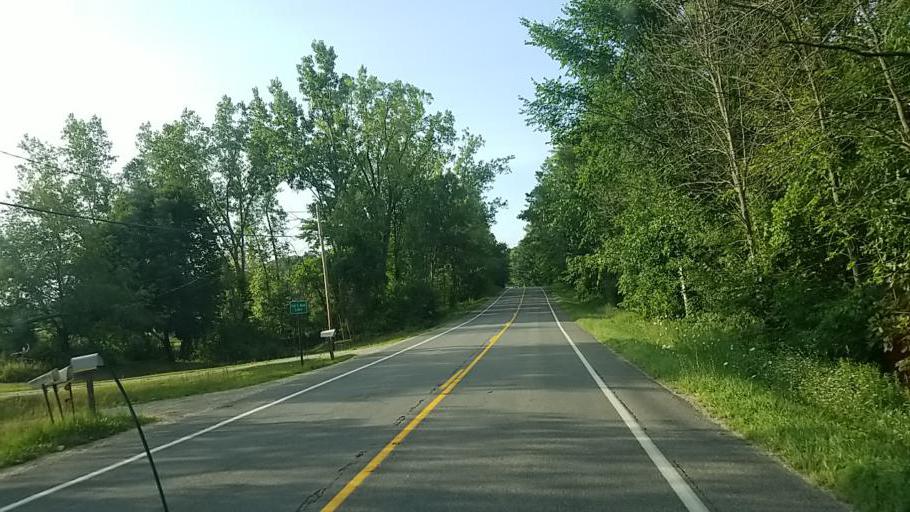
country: US
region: Michigan
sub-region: Montcalm County
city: Greenville
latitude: 43.1263
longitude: -85.3520
